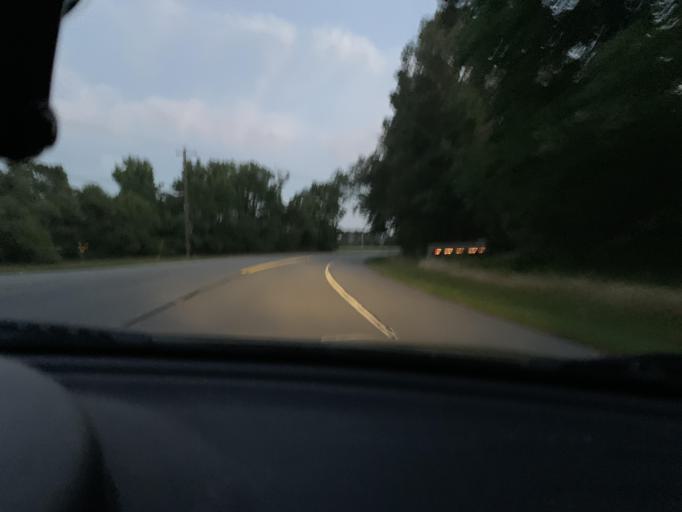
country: US
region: Maryland
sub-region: Talbot County
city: Saint Michaels
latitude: 38.7579
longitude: -76.3193
